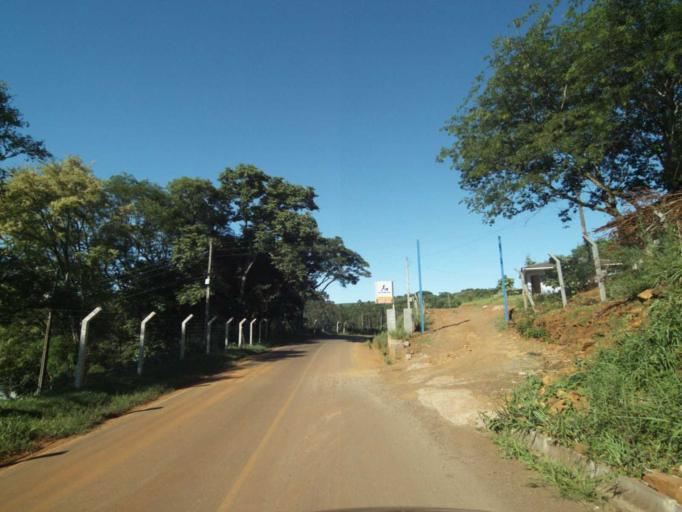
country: BR
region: Parana
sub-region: Coronel Vivida
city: Coronel Vivida
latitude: -25.9650
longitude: -52.8025
